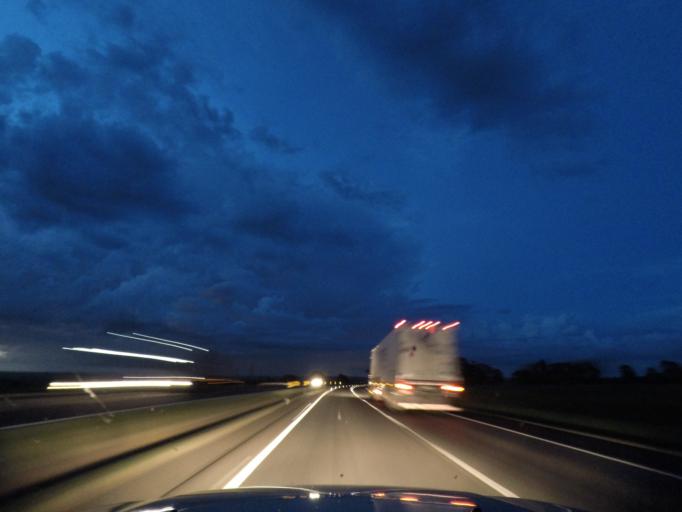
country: BR
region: Minas Gerais
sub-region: Uberlandia
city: Uberlandia
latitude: -19.2398
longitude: -48.1399
